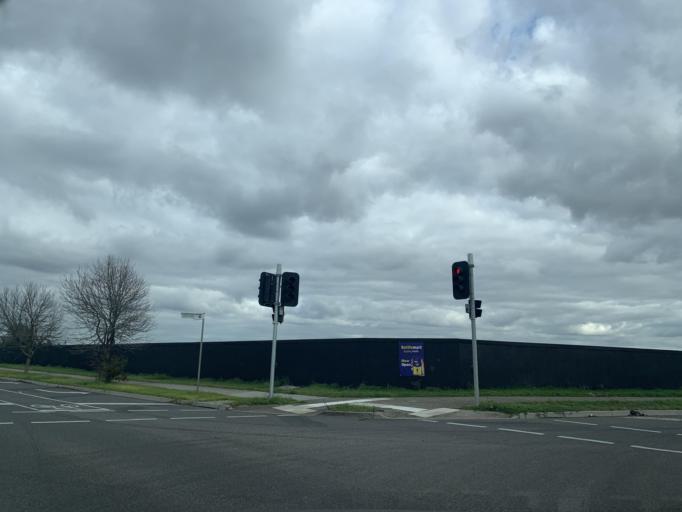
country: AU
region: Victoria
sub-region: Whittlesea
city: Epping
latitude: -37.6186
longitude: 145.0048
